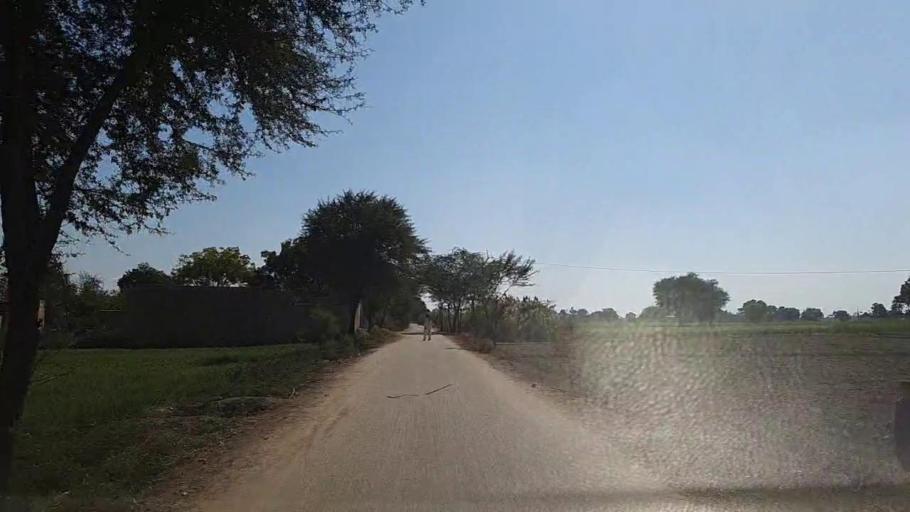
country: PK
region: Sindh
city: Nawabshah
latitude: 26.2385
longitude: 68.4457
